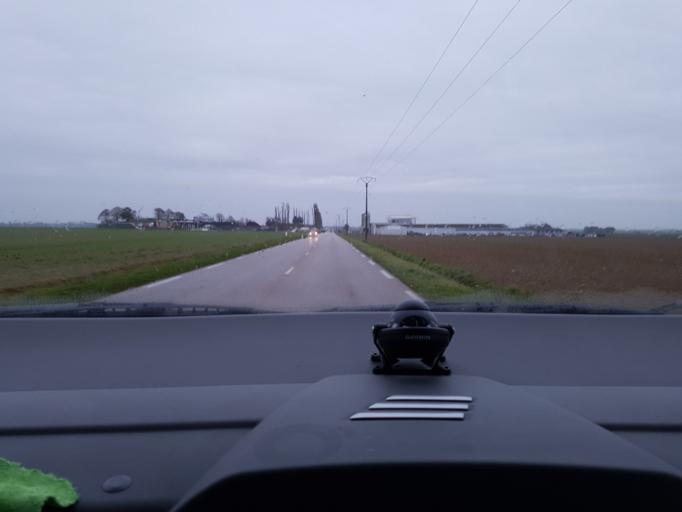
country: FR
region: Haute-Normandie
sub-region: Departement de l'Eure
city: Le Neubourg
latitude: 49.1481
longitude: 0.9315
